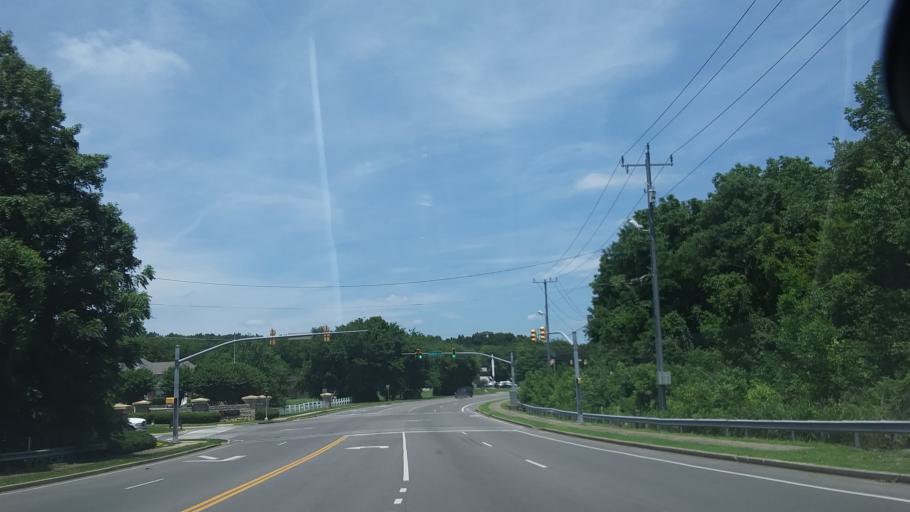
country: US
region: Tennessee
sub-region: Rutherford County
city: La Vergne
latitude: 36.0885
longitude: -86.6275
